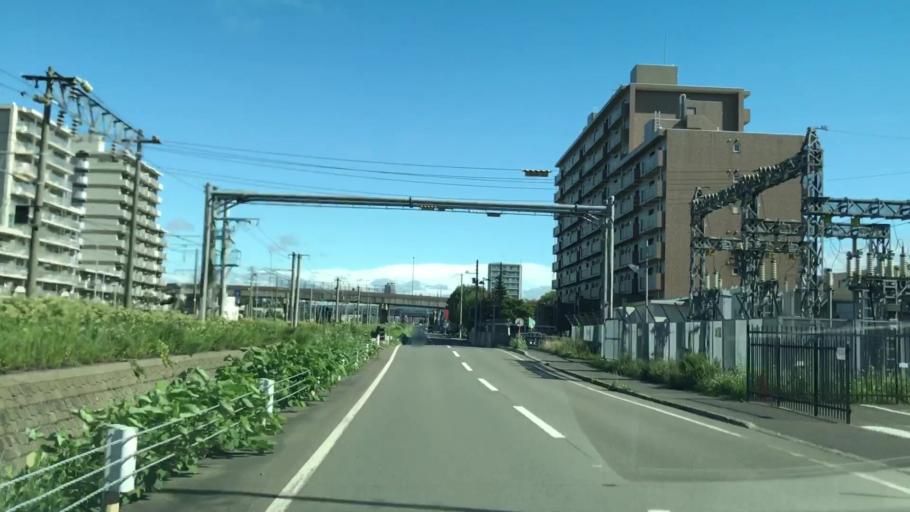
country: JP
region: Hokkaido
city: Sapporo
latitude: 43.0967
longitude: 141.2821
